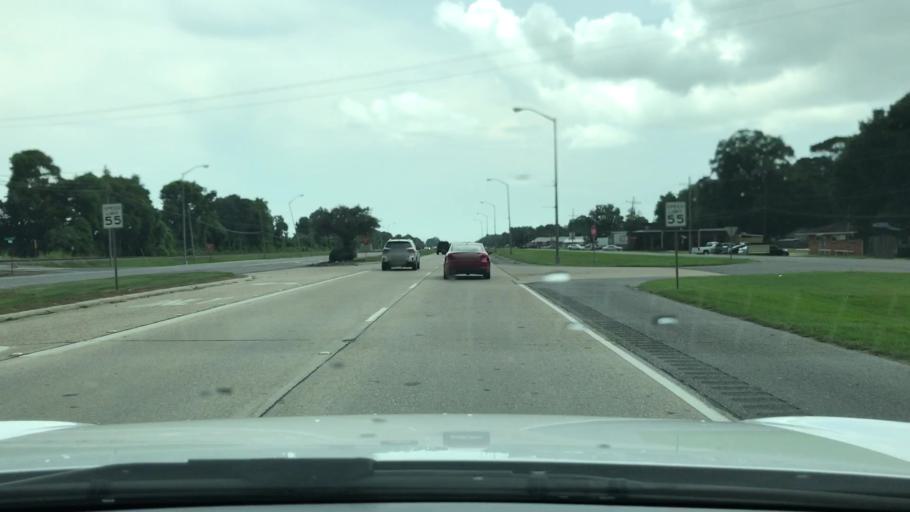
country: US
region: Louisiana
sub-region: Iberville Parish
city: Plaquemine
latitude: 30.3036
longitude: -91.2440
